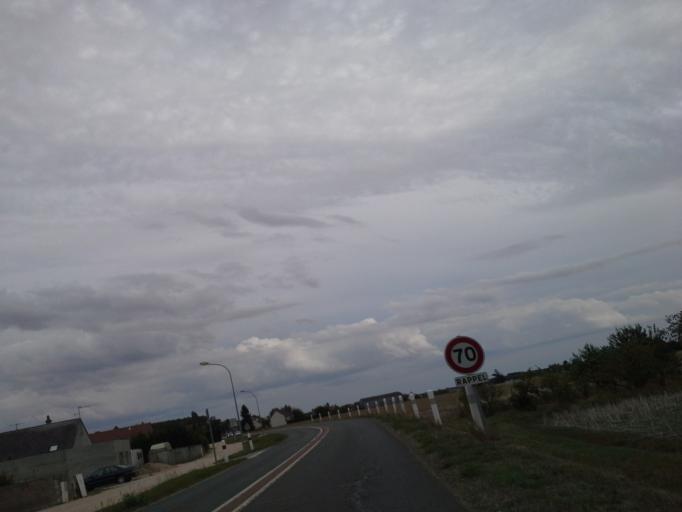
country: FR
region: Centre
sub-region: Departement du Loir-et-Cher
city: Villiers-sur-Loir
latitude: 47.8076
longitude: 0.9865
